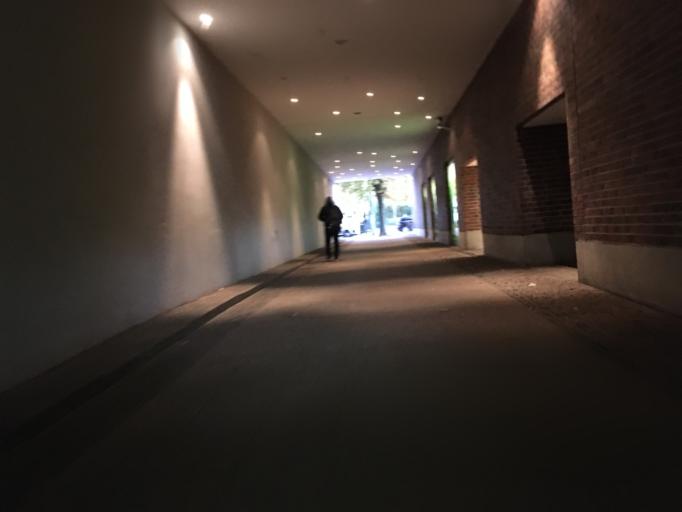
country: DE
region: Berlin
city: Pankow
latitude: 52.5706
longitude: 13.4055
